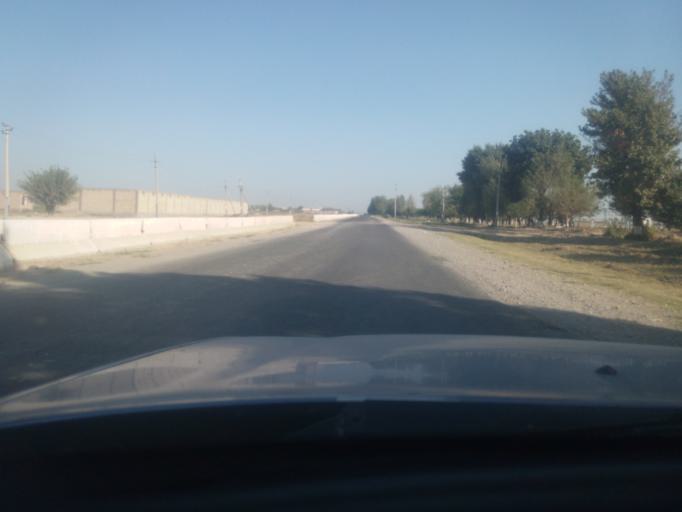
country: UZ
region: Sirdaryo
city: Guliston
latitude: 40.5045
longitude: 68.7972
